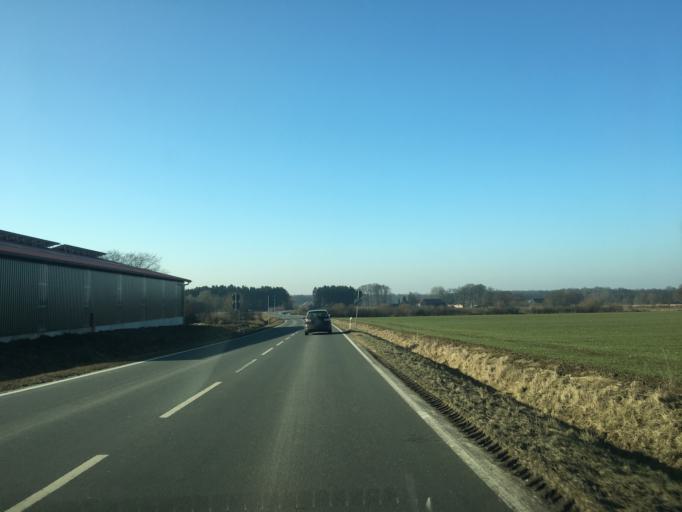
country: DE
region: North Rhine-Westphalia
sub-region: Regierungsbezirk Munster
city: Billerbeck
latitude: 52.0281
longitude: 7.2846
